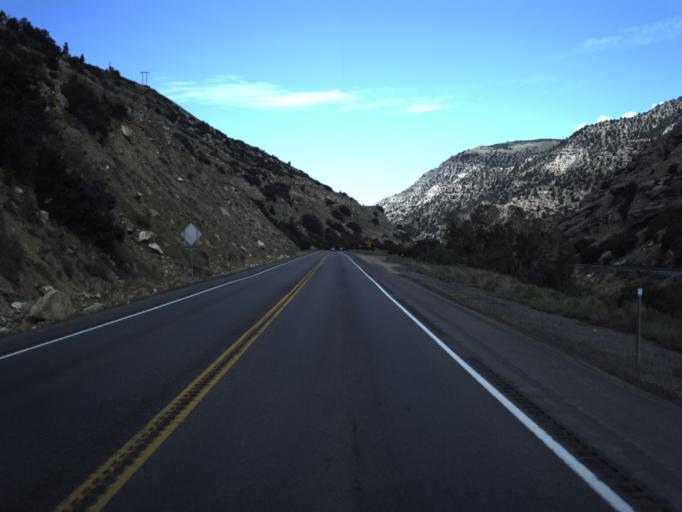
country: US
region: Utah
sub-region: Carbon County
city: Helper
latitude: 39.7659
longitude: -110.9046
